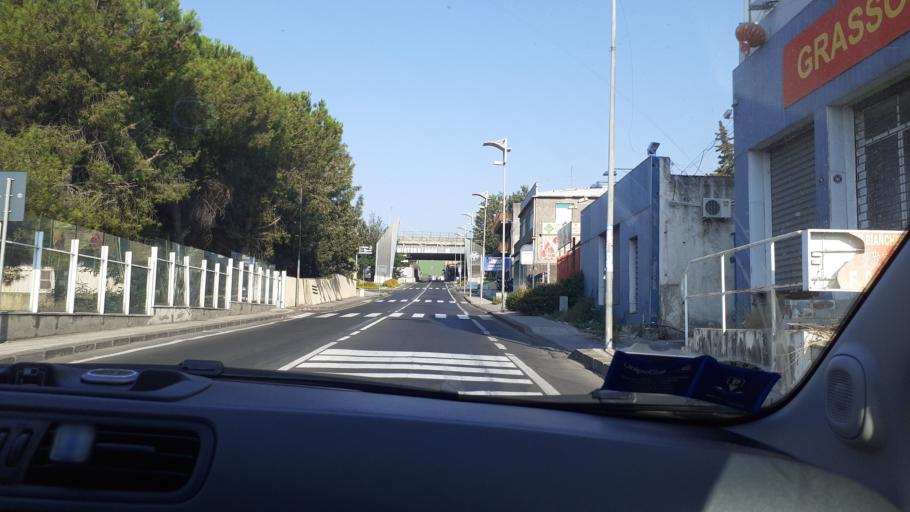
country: IT
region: Sicily
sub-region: Catania
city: Misterbianco
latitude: 37.5154
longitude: 15.0218
